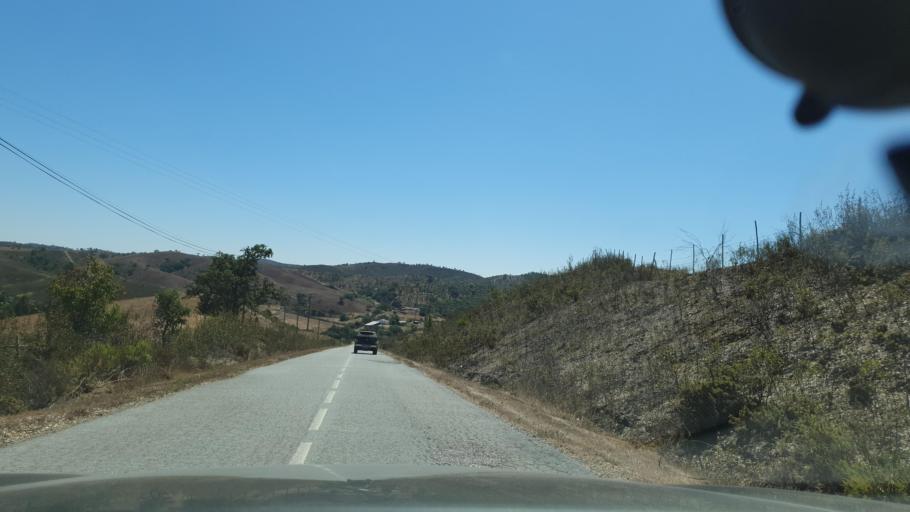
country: PT
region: Faro
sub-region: Monchique
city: Monchique
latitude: 37.4340
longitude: -8.5663
